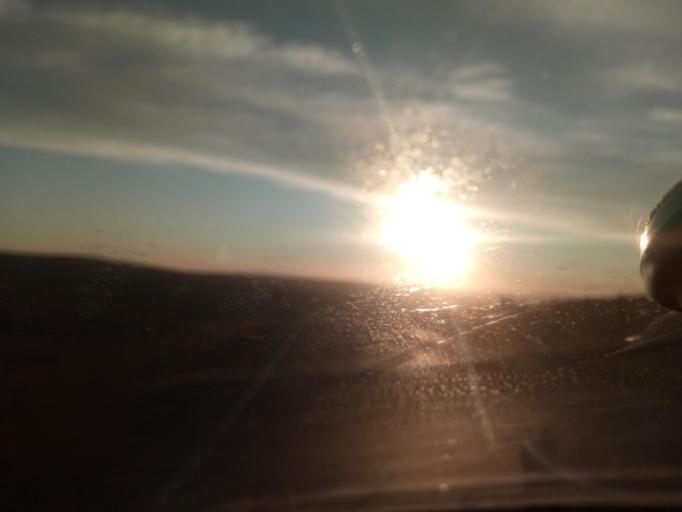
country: GB
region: England
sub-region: Northumberland
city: Bardon Mill
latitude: 54.7847
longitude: -2.3244
